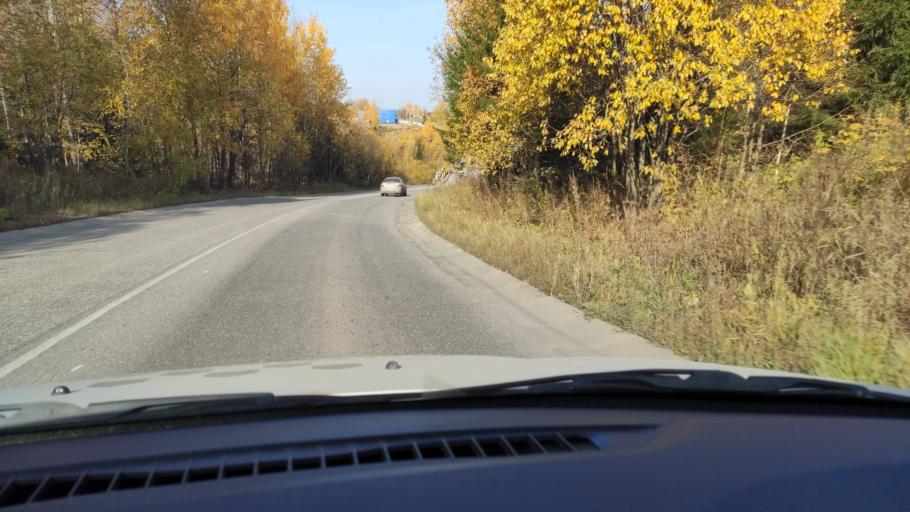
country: RU
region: Perm
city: Novyye Lyady
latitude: 58.0411
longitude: 56.5984
